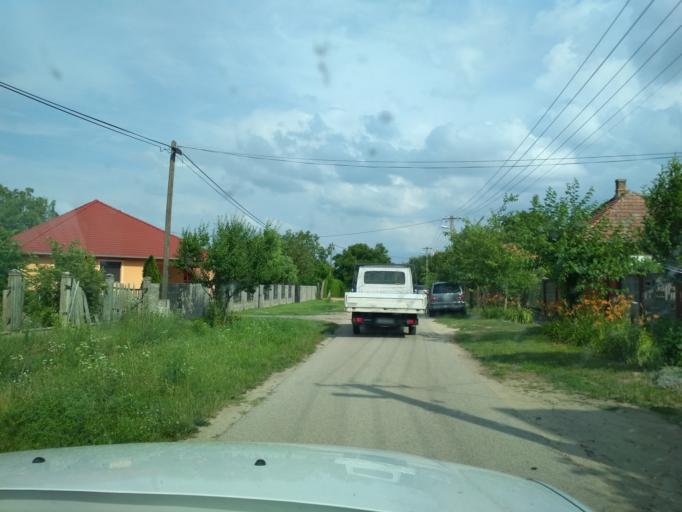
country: HU
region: Pest
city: Tapioszentmarton
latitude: 47.3321
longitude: 19.7530
